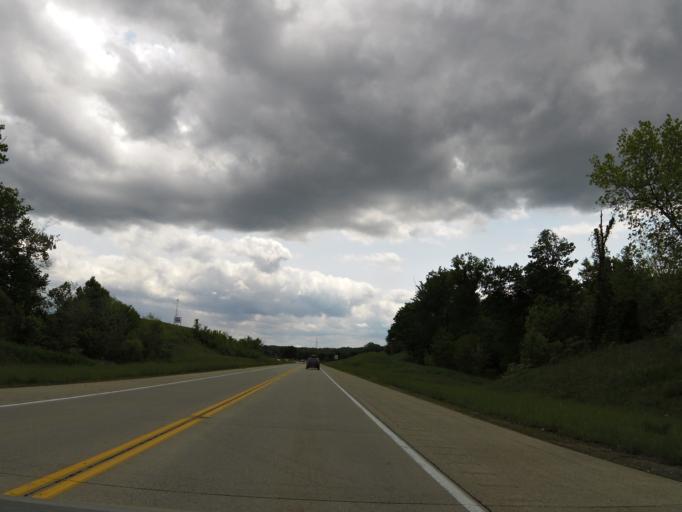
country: US
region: Ohio
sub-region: Meigs County
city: Pomeroy
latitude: 39.1591
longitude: -82.0357
